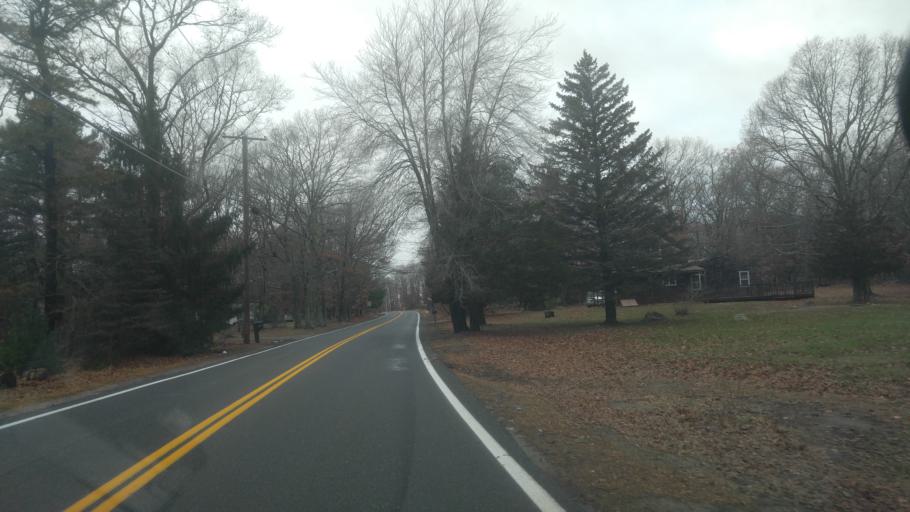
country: US
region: Rhode Island
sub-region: Kent County
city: West Warwick
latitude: 41.6537
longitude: -71.5448
